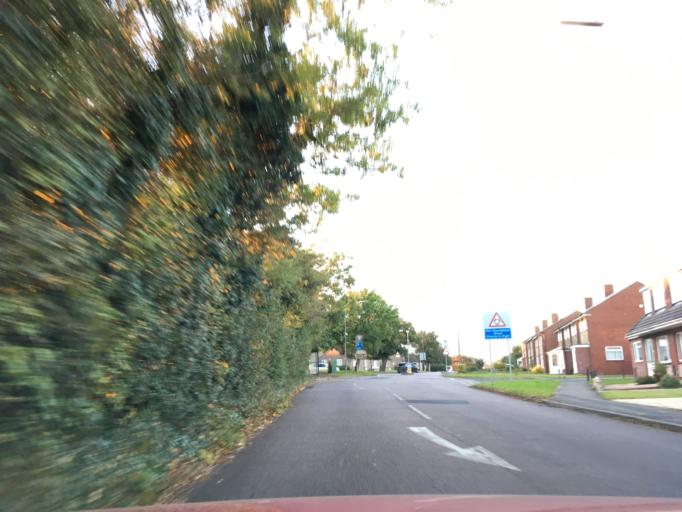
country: GB
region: England
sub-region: South Gloucestershire
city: Stoke Gifford
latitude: 51.5294
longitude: -2.5596
